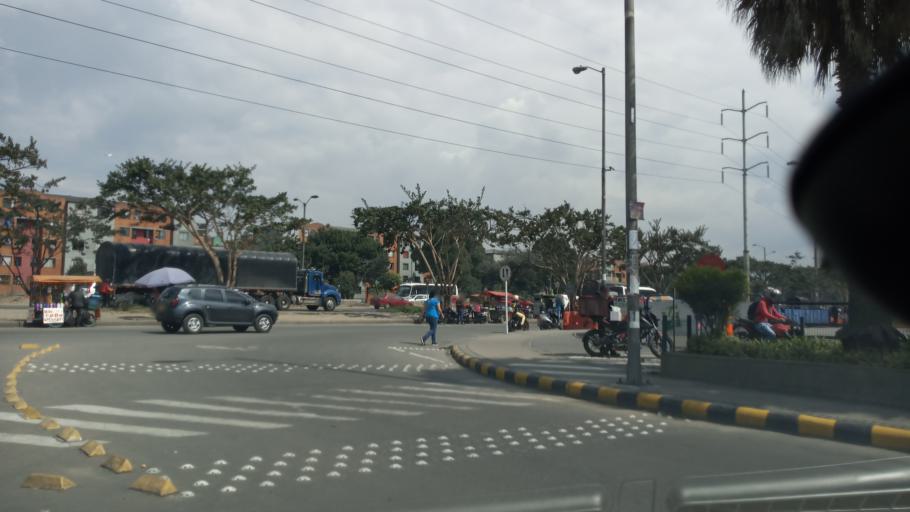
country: CO
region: Cundinamarca
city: Funza
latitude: 4.6765
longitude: -74.1541
